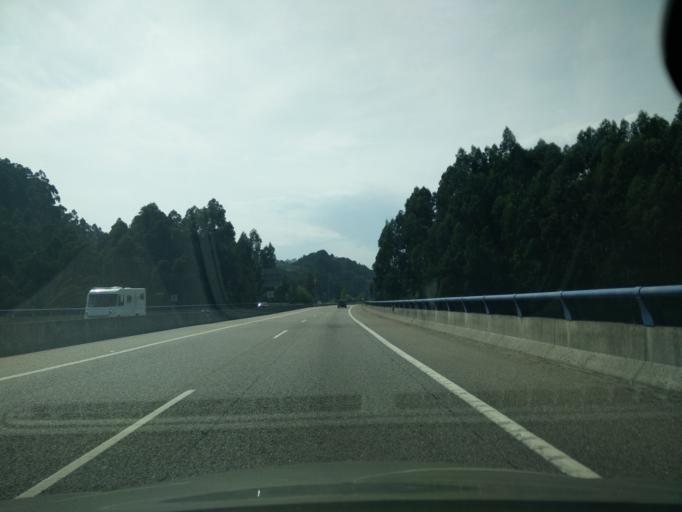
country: ES
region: Asturias
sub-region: Province of Asturias
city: Ribadesella
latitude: 43.4351
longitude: -5.0619
